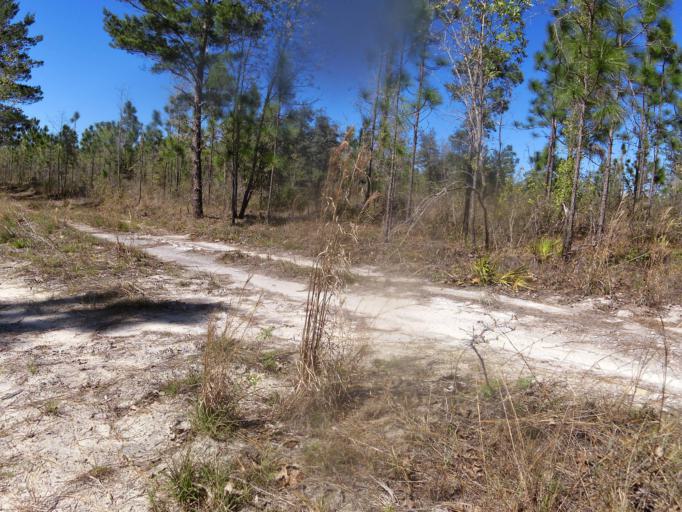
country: US
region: Florida
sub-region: Clay County
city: Keystone Heights
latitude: 29.8377
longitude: -81.9812
